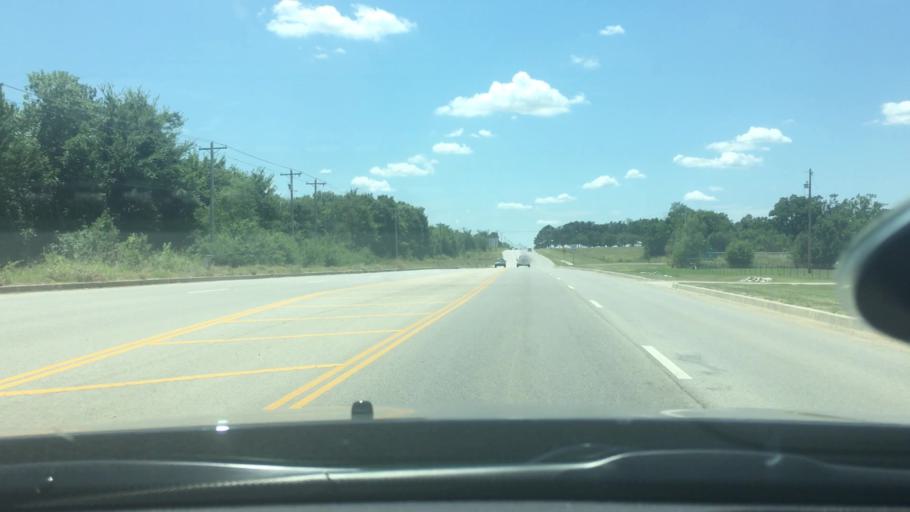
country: US
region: Oklahoma
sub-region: Bryan County
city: Calera
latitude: 33.9619
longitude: -96.3990
